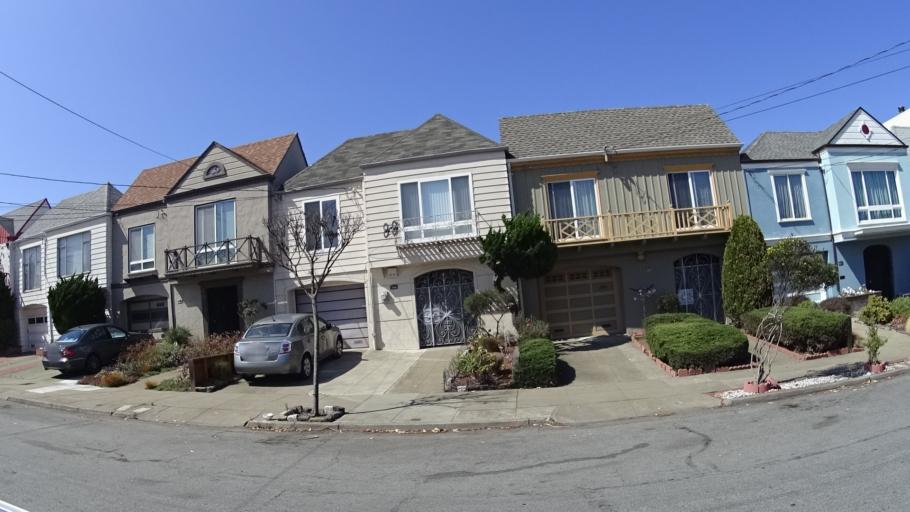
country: US
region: California
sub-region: San Mateo County
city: Daly City
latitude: 37.7510
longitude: -122.4891
